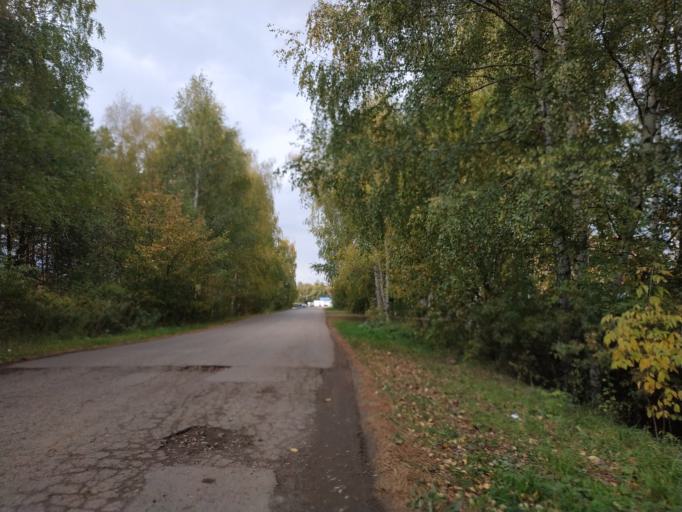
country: RU
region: Chuvashia
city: Ishley
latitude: 56.1302
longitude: 47.0887
